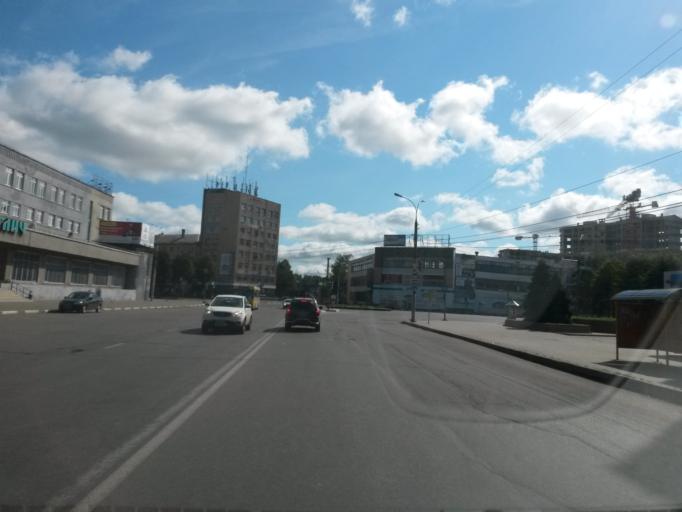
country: RU
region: Jaroslavl
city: Yaroslavl
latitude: 57.6294
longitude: 39.8468
